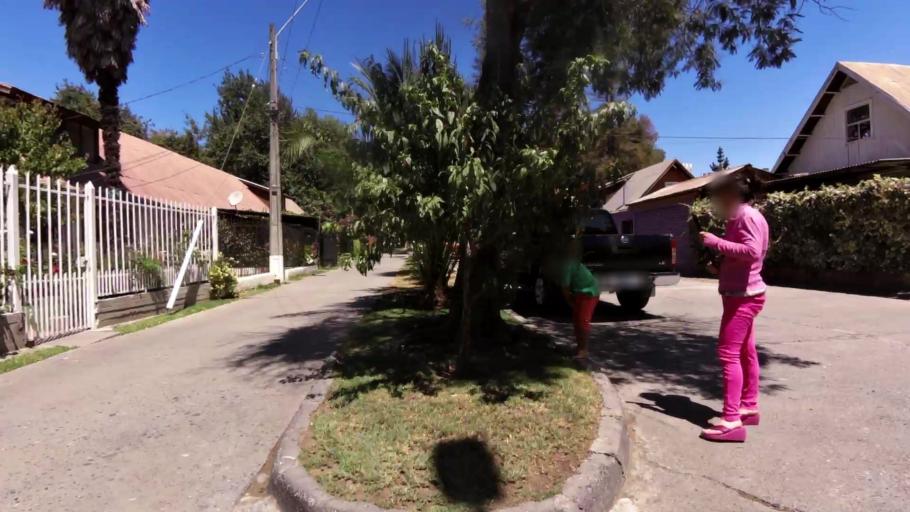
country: CL
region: O'Higgins
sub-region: Provincia de Cachapoal
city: Rancagua
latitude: -34.1658
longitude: -70.7546
